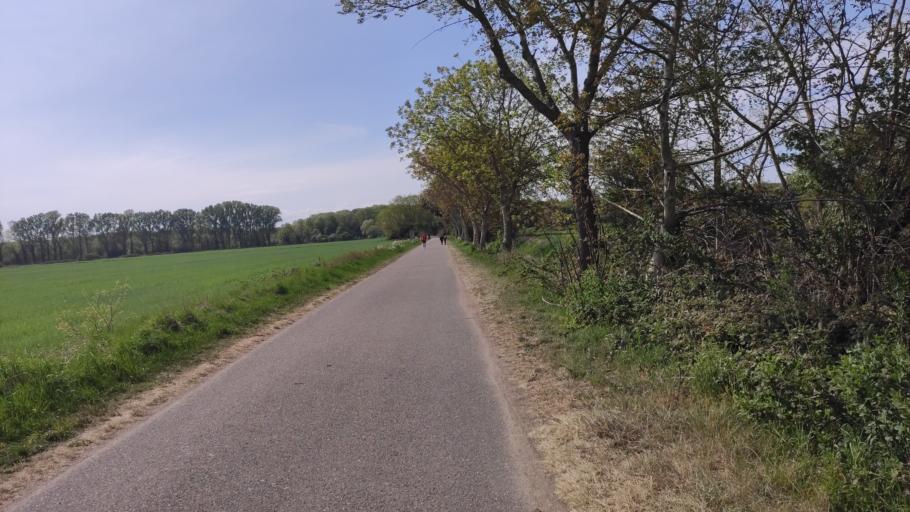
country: DE
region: Baden-Wuerttemberg
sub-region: Freiburg Region
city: Umkirch
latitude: 48.0095
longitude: 7.7759
